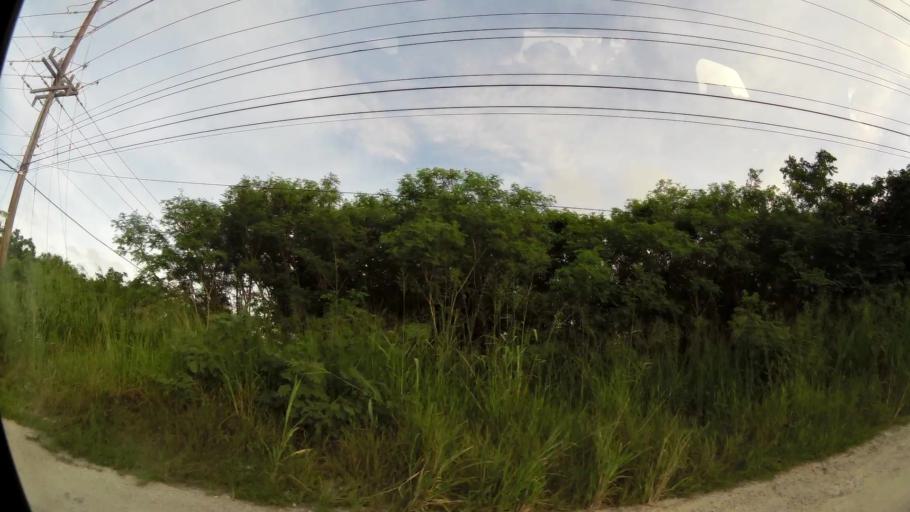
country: BB
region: Saint Philip
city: Crane
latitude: 13.0872
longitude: -59.4920
